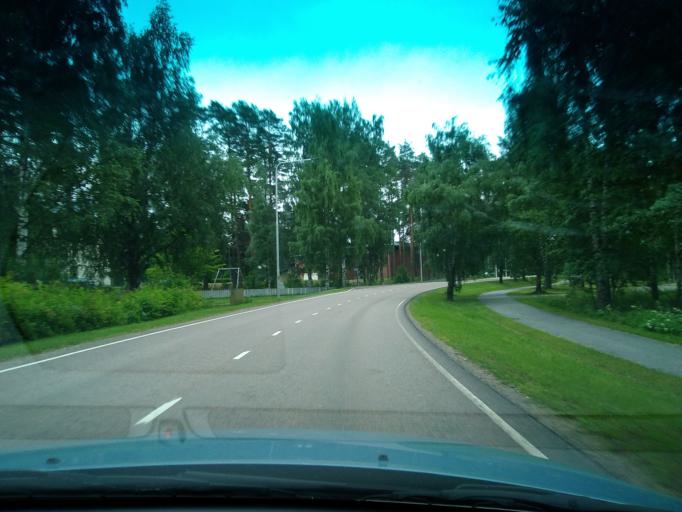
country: FI
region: Central Finland
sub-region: Keuruu
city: Multia
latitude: 62.4054
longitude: 24.7924
